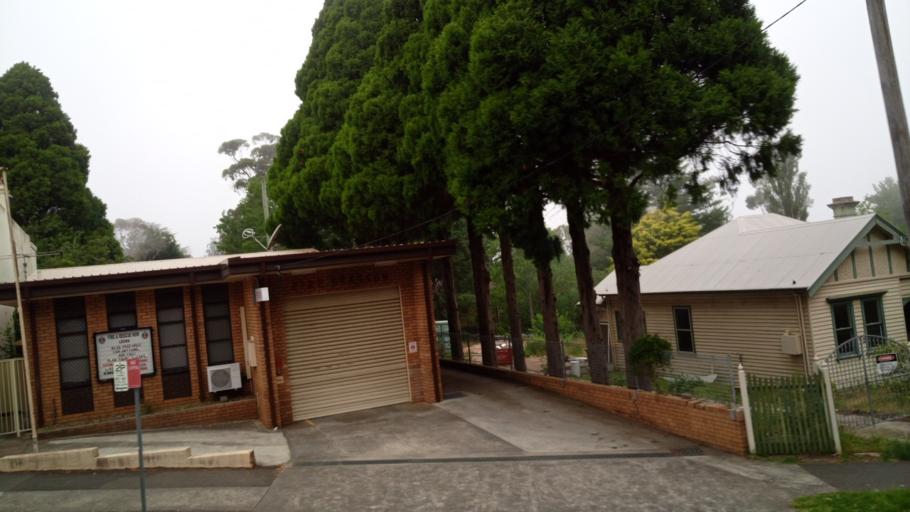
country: AU
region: New South Wales
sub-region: Blue Mountains Municipality
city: Leura
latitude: -33.7144
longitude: 150.3306
